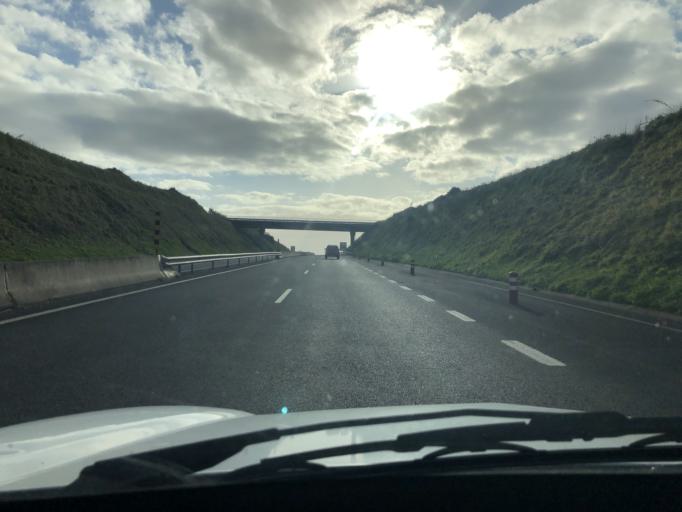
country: PT
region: Azores
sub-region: Ribeira Grande
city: Rabo de Peixe
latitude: 37.7312
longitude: -25.5393
